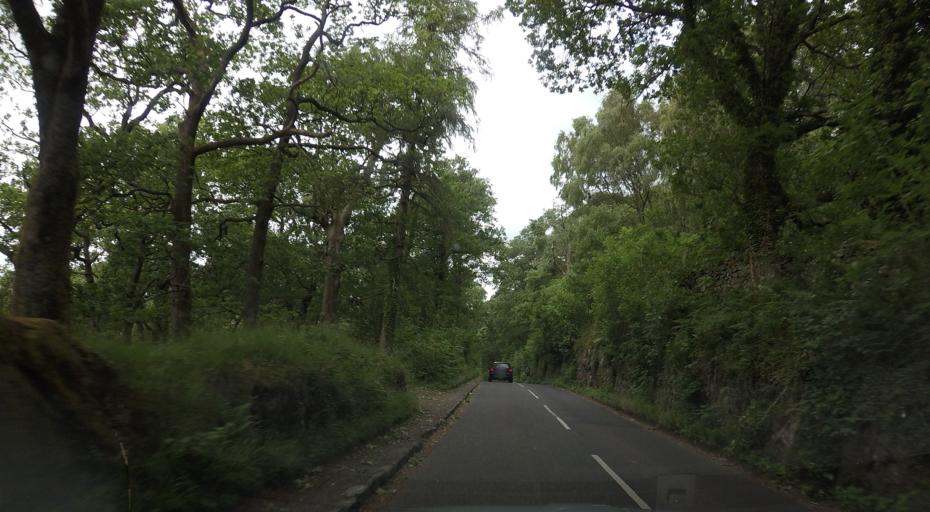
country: GB
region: England
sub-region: Cumbria
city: Keswick
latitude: 54.5776
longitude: -3.1315
